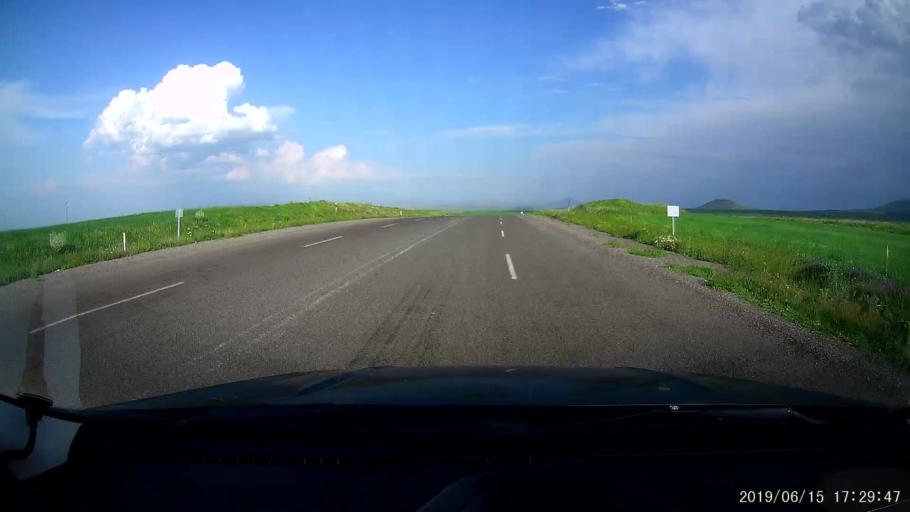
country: TR
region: Kars
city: Basgedikler
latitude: 40.5872
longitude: 43.4581
